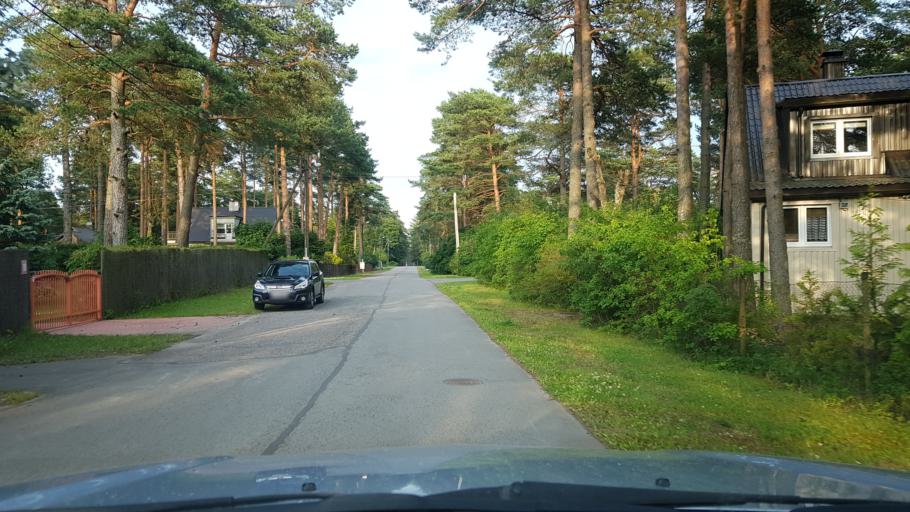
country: EE
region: Ida-Virumaa
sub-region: Narva-Joesuu linn
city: Narva-Joesuu
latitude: 59.4563
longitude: 28.0525
